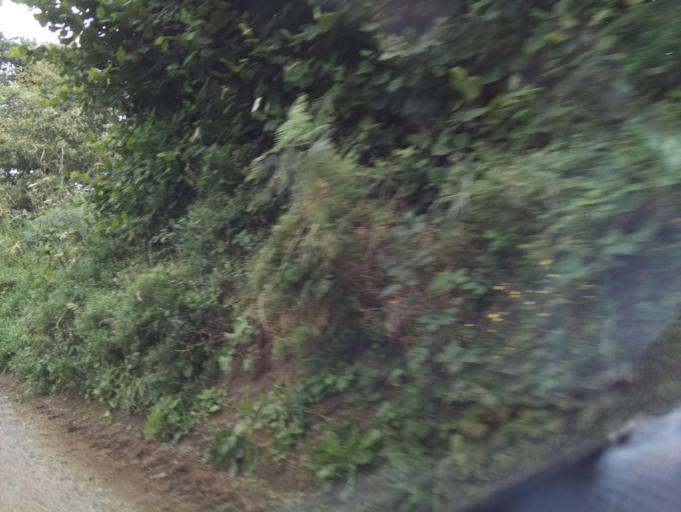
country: GB
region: England
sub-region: Devon
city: South Brent
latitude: 50.3992
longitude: -3.8331
